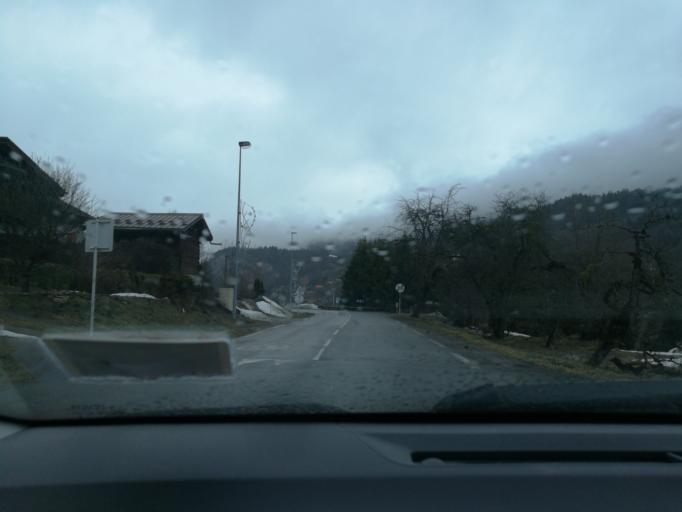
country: FR
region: Rhone-Alpes
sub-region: Departement de la Haute-Savoie
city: Araches-la-Frasse
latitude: 46.0439
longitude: 6.6321
